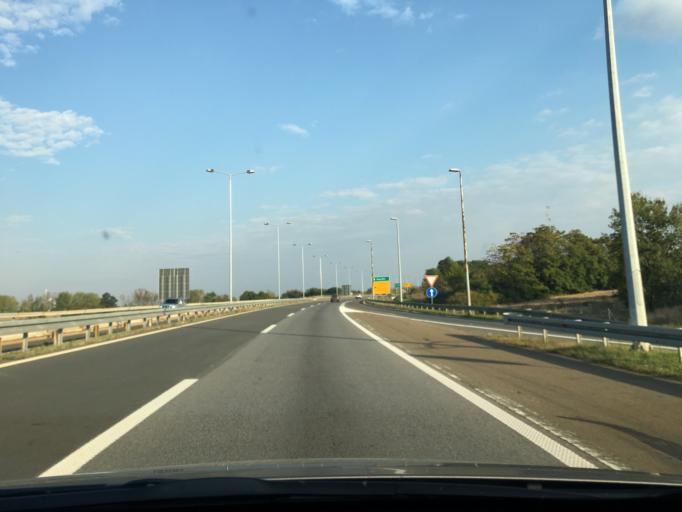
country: RS
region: Central Serbia
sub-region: Podunavski Okrug
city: Smederevo
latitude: 44.5840
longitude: 20.9687
